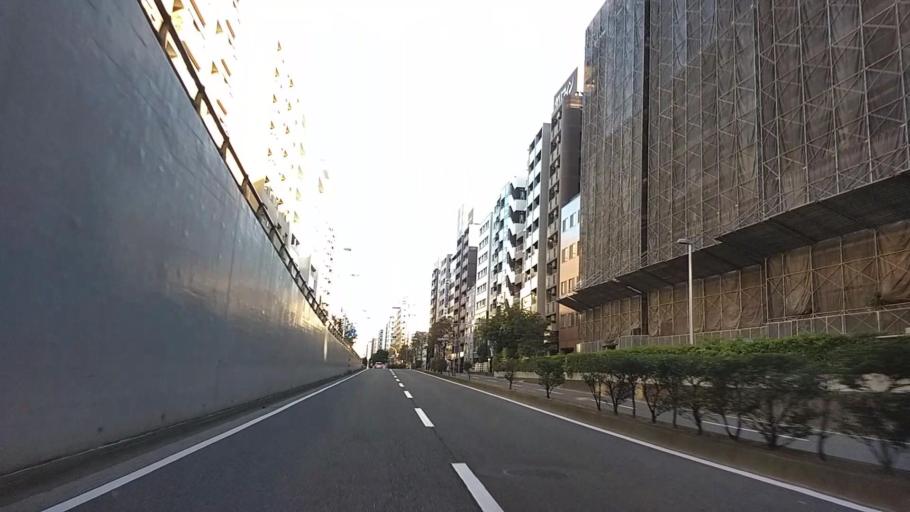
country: JP
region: Kanagawa
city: Yokohama
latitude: 35.4528
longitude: 139.6283
